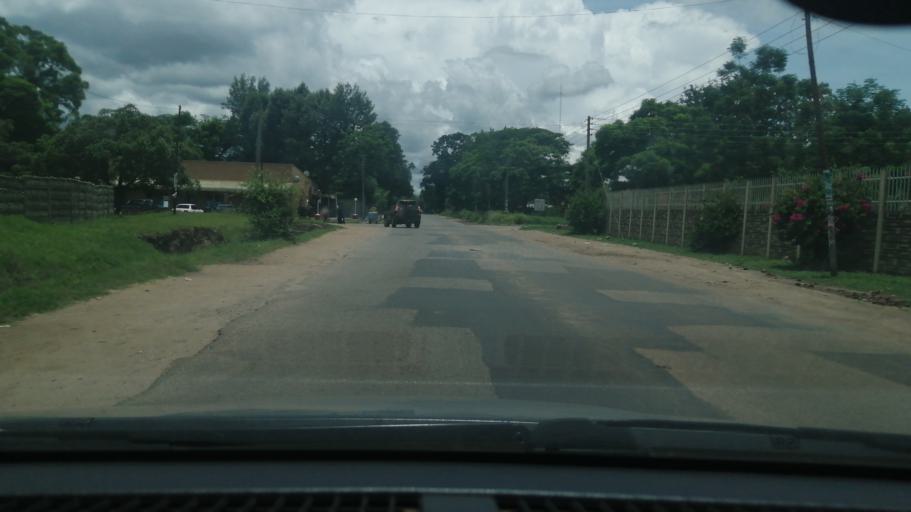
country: ZW
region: Harare
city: Harare
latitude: -17.8854
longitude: 31.0717
